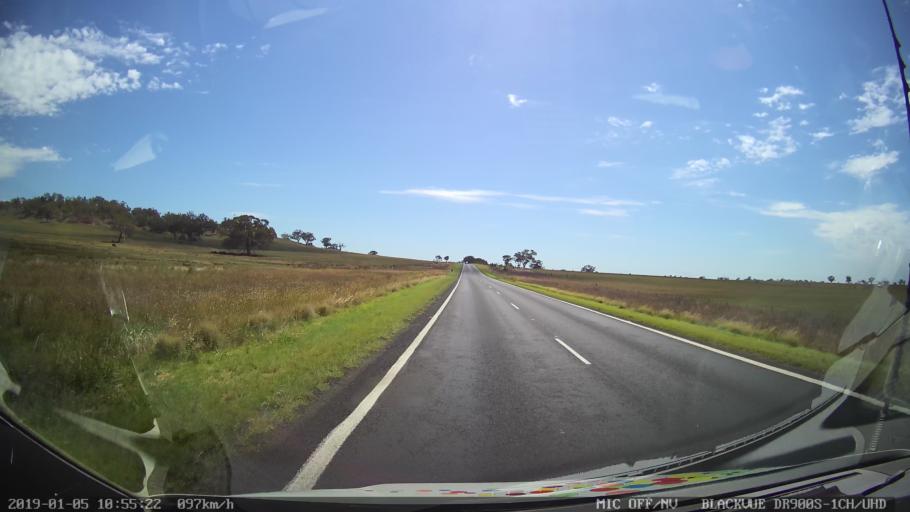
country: AU
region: New South Wales
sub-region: Warrumbungle Shire
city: Coonabarabran
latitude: -31.4487
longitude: 149.1426
